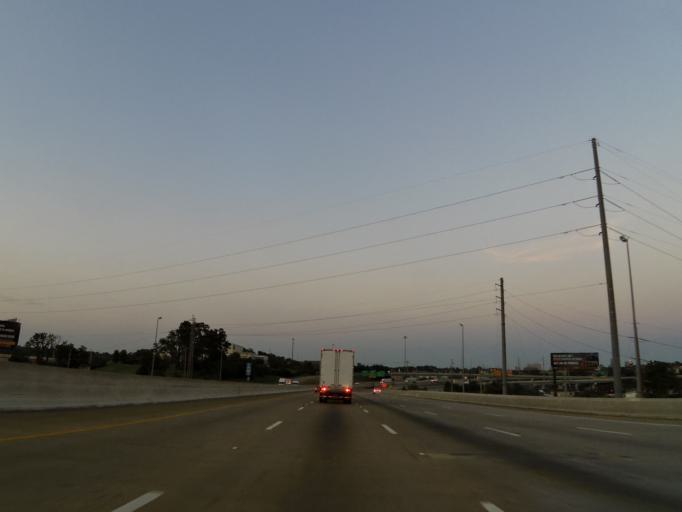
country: US
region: Tennessee
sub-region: Knox County
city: Knoxville
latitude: 35.9619
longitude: -83.9535
